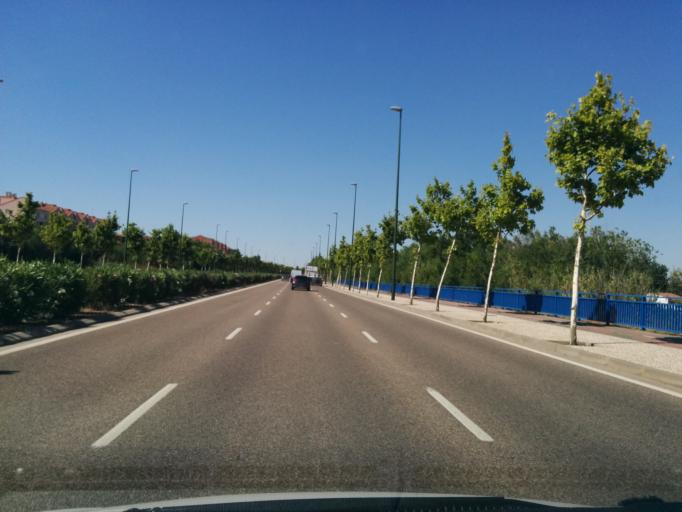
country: ES
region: Aragon
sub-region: Provincia de Zaragoza
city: Zaragoza
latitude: 41.6402
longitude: -0.8583
